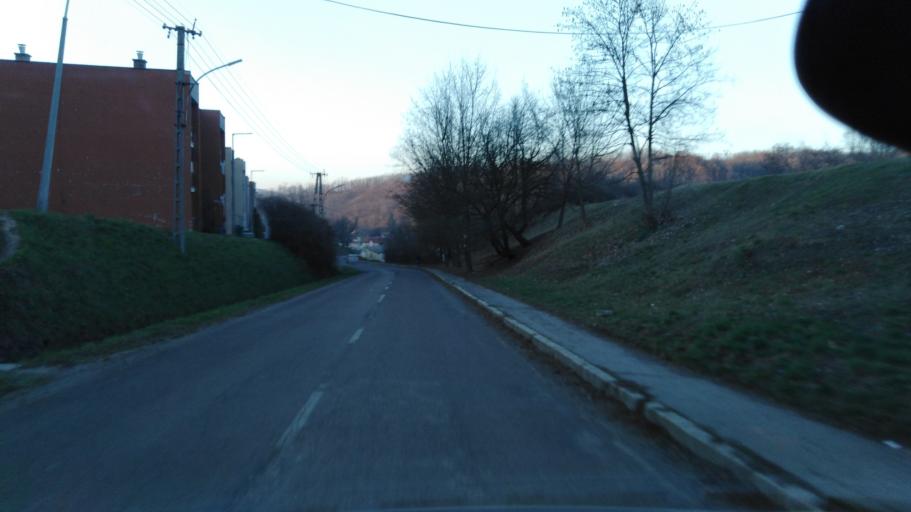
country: HU
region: Nograd
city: Salgotarjan
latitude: 48.0869
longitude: 19.8094
